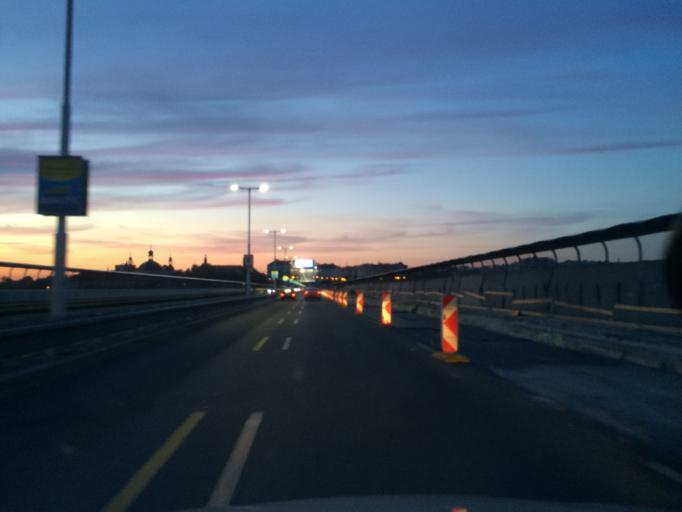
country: CZ
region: Praha
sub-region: Praha 2
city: Vysehrad
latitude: 50.0640
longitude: 14.4306
